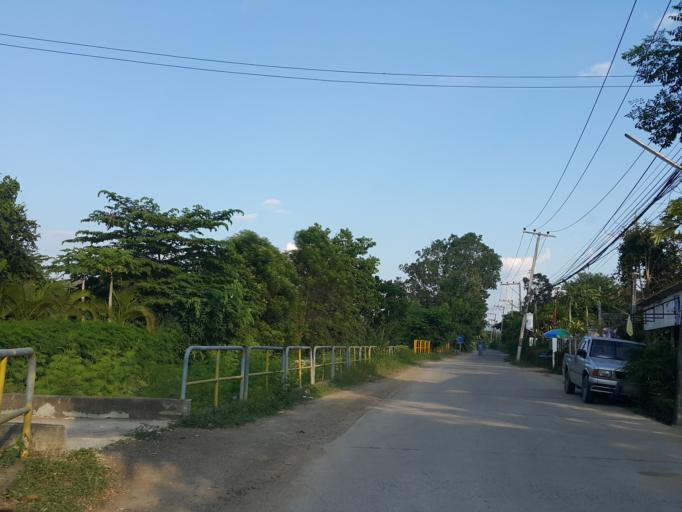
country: TH
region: Chiang Mai
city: San Kamphaeng
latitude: 18.7457
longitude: 99.0971
